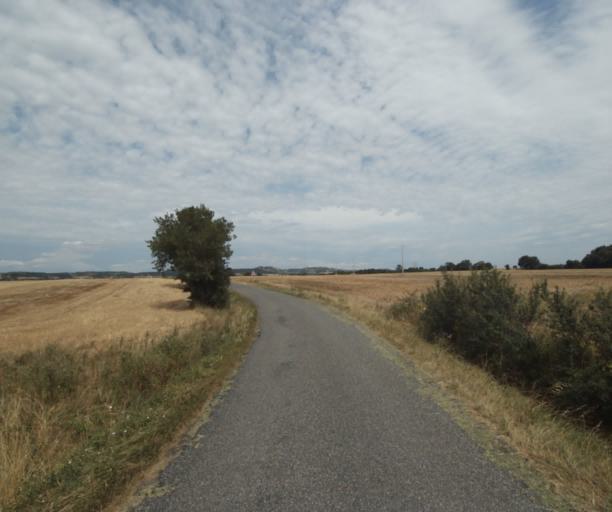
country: FR
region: Midi-Pyrenees
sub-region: Departement de la Haute-Garonne
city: Saint-Felix-Lauragais
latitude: 43.4003
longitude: 1.9083
